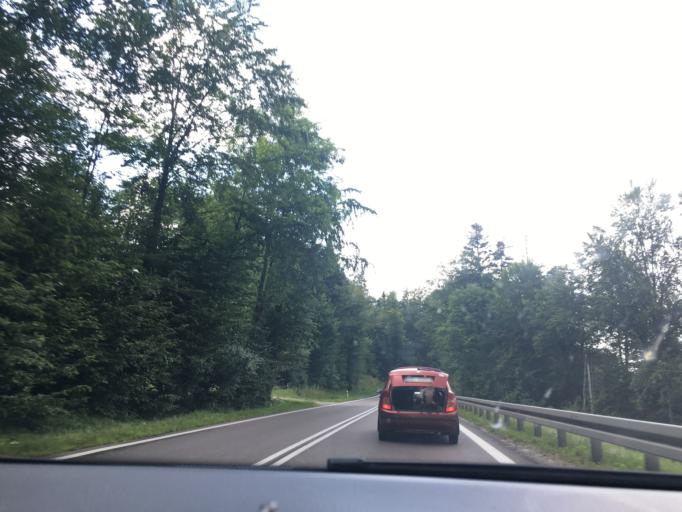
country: PL
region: Subcarpathian Voivodeship
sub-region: Powiat brzozowski
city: Jablonica Polska
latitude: 49.7257
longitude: 21.9090
